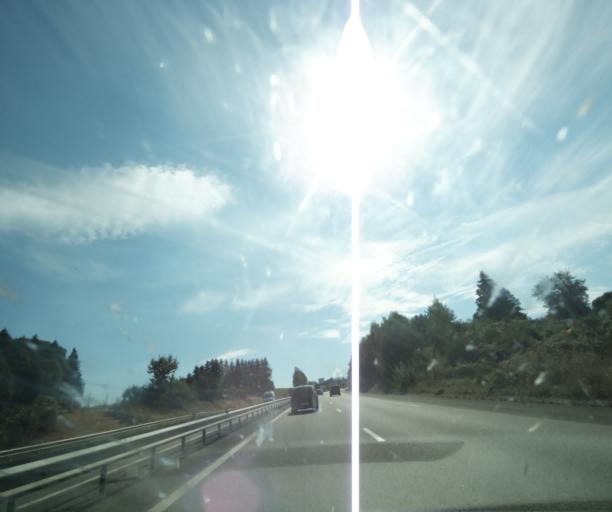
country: FR
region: Limousin
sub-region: Departement de la Correze
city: Sainte-Fereole
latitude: 45.2915
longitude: 1.5736
